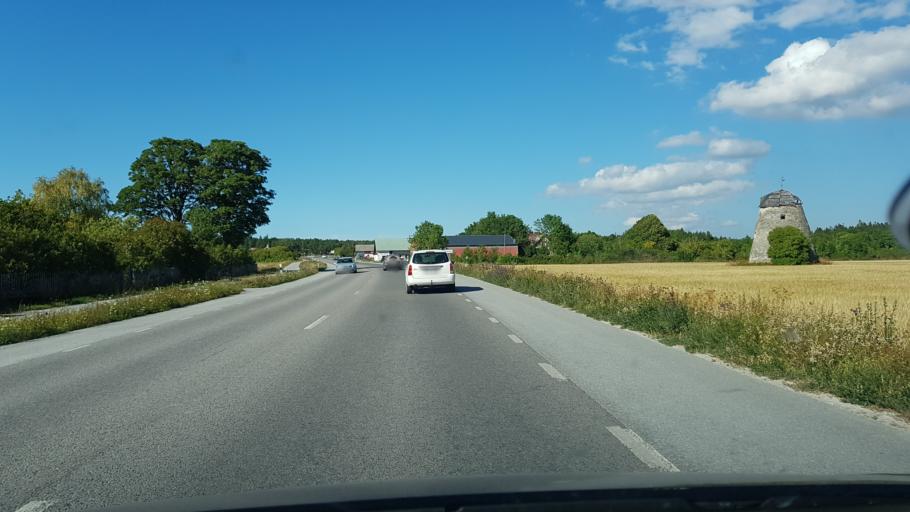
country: SE
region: Gotland
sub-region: Gotland
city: Vibble
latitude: 57.5282
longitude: 18.1757
